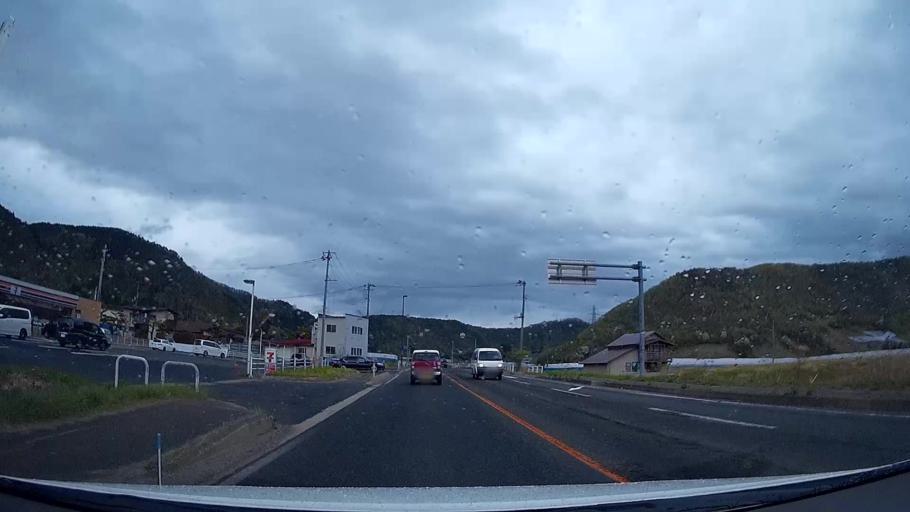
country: JP
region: Yamagata
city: Takahata
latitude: 38.0807
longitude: 140.1856
